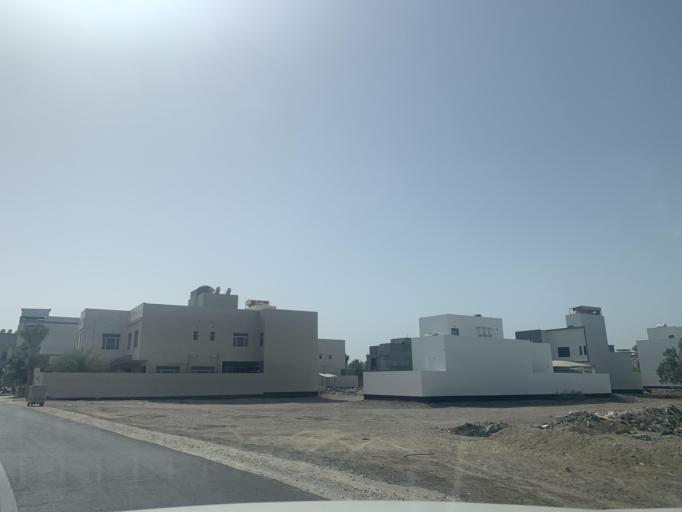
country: BH
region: Northern
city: Sitrah
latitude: 26.1679
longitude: 50.6283
